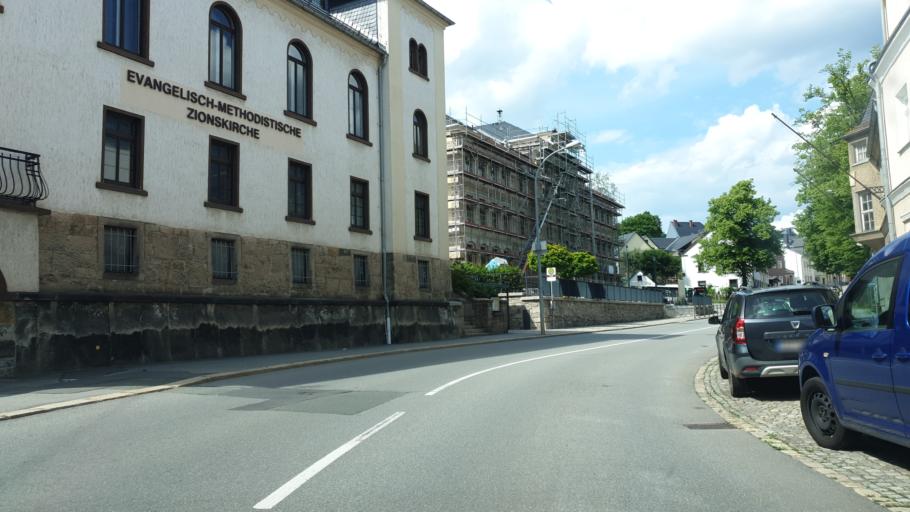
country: DE
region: Saxony
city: Schwarzenberg
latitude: 50.5356
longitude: 12.7821
